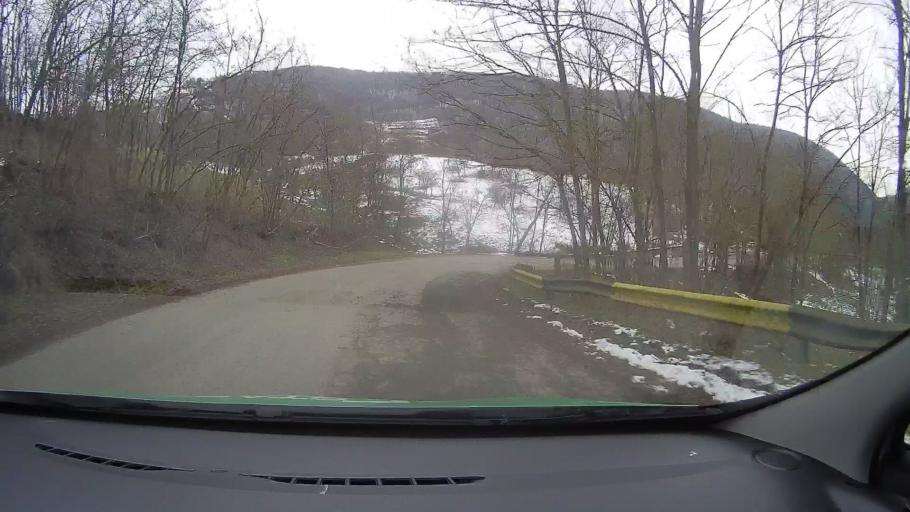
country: RO
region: Hunedoara
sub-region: Comuna Balsa
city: Balsa
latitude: 46.0172
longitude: 23.1481
